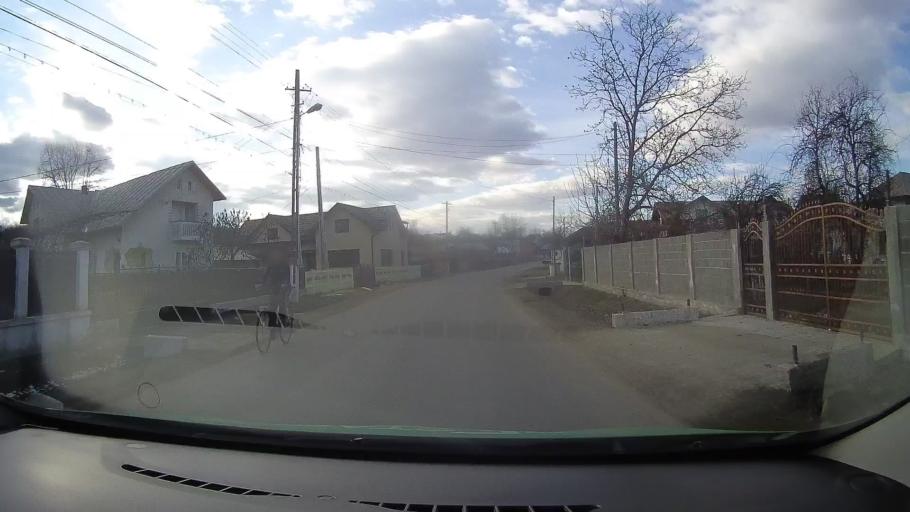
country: RO
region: Dambovita
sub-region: Comuna Ulmi
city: Ulmi
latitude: 44.8838
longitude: 25.5124
